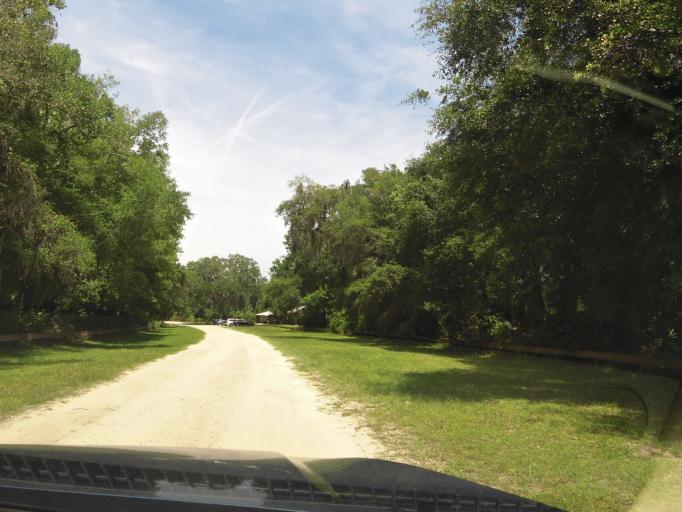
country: US
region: Florida
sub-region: Duval County
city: Atlantic Beach
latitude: 30.4851
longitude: -81.4904
